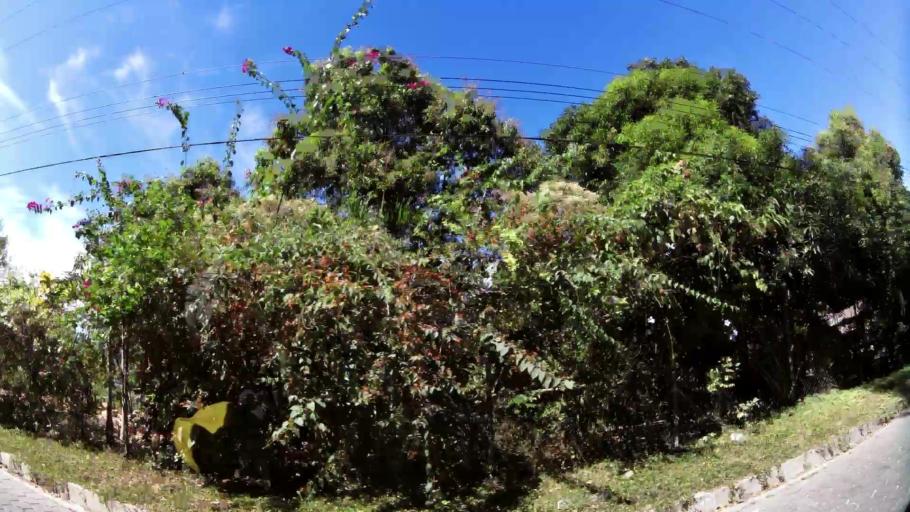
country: SV
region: San Salvador
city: Apopa
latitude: 13.8072
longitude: -89.1739
